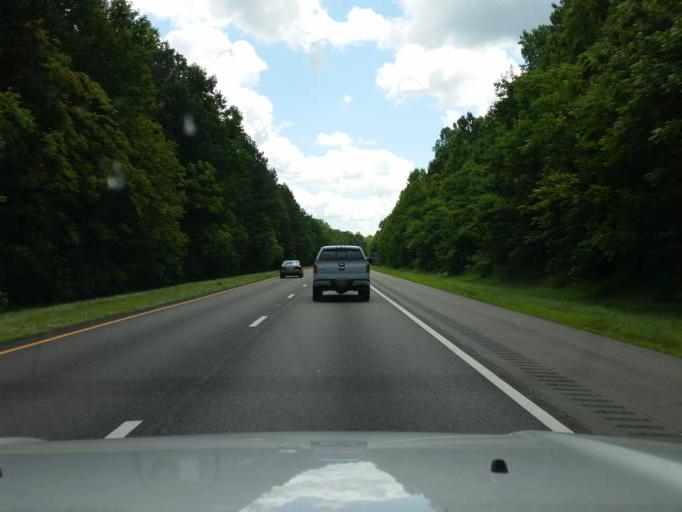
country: US
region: Virginia
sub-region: King William County
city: West Point
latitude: 37.4050
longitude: -76.7863
